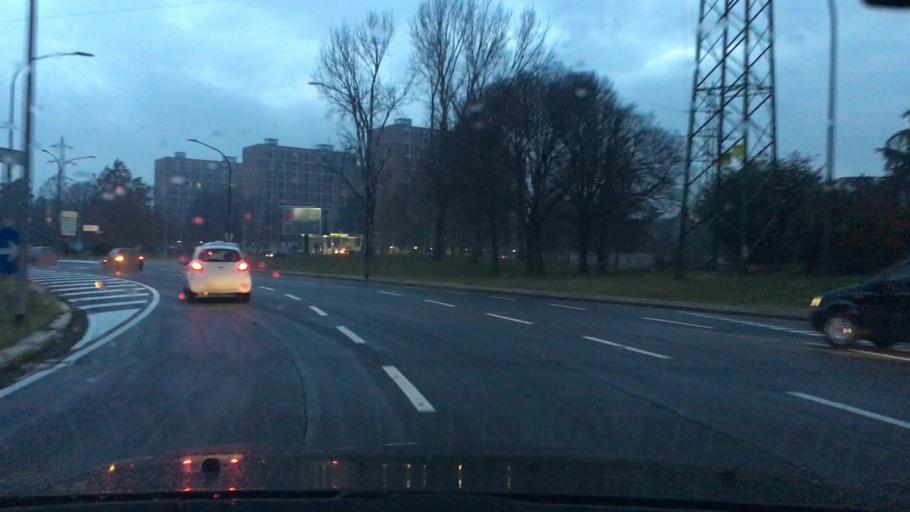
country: IT
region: Emilia-Romagna
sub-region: Provincia di Bologna
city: Casalecchio di Reno
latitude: 44.4923
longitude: 11.2892
